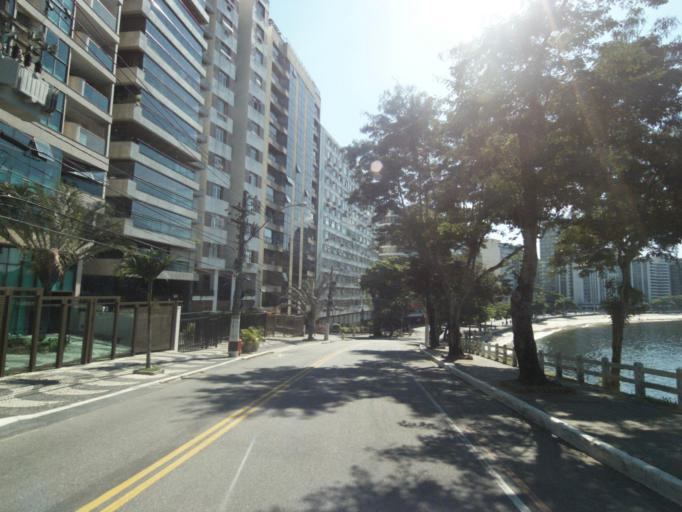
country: BR
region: Rio de Janeiro
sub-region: Niteroi
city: Niteroi
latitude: -22.9057
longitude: -43.1253
